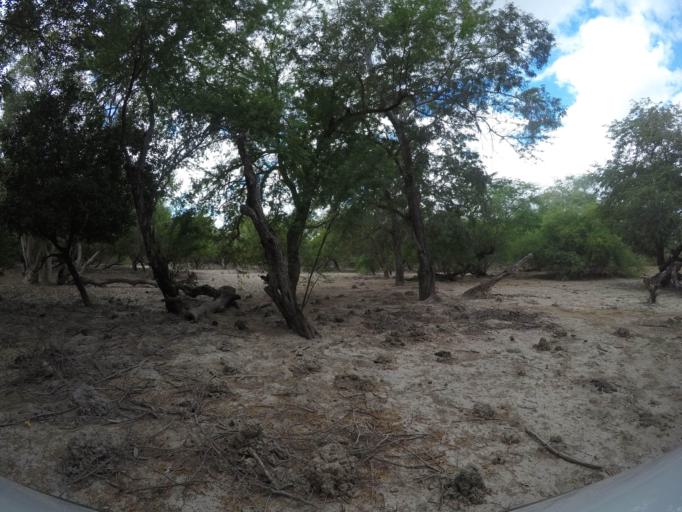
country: TL
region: Lautem
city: Lospalos
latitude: -8.3716
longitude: 126.8861
